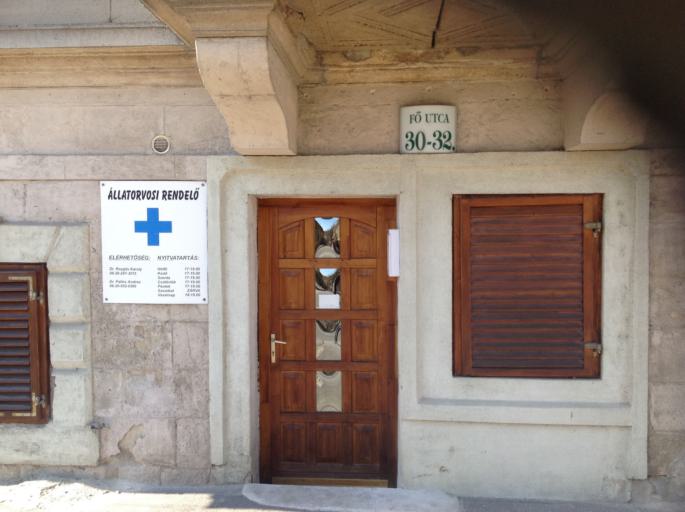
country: HU
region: Pest
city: Soskut
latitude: 47.4080
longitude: 18.8316
